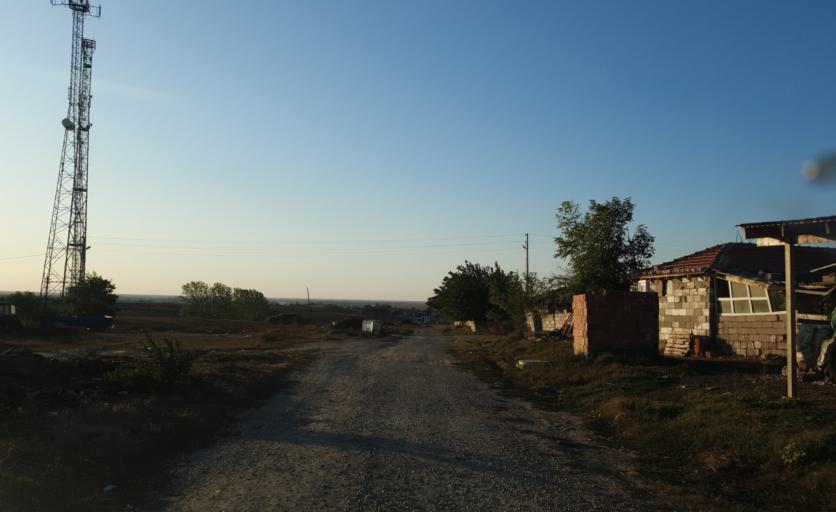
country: TR
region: Tekirdag
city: Beyazkoy
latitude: 41.3298
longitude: 27.7448
